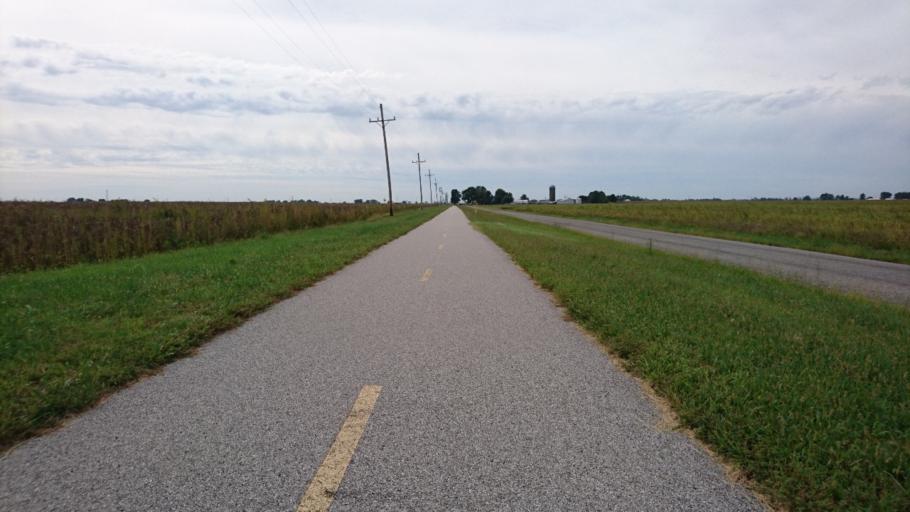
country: US
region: Illinois
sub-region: Madison County
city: Worden
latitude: 38.9163
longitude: -89.8374
